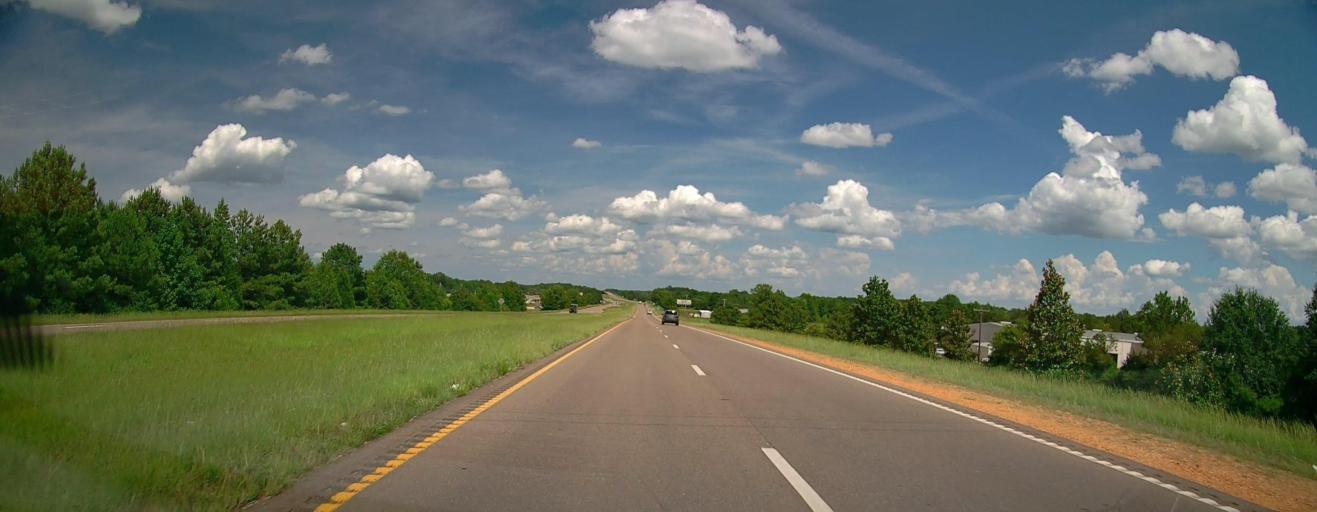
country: US
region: Mississippi
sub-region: Monroe County
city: Aberdeen
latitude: 33.8154
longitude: -88.5375
